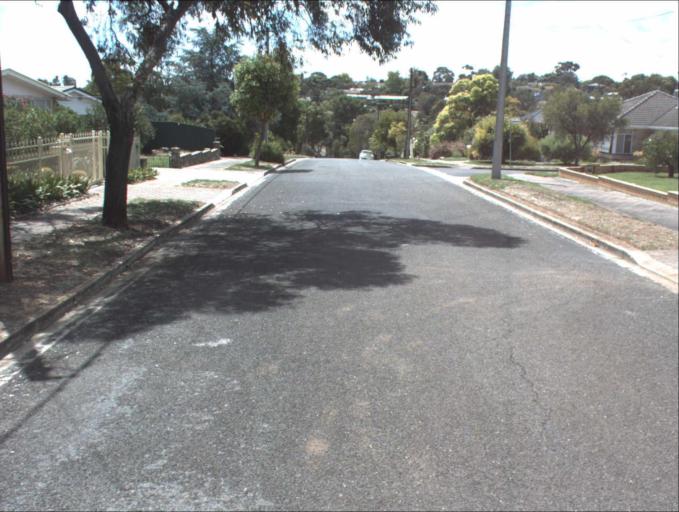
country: AU
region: South Australia
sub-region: Port Adelaide Enfield
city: Gilles Plains
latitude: -34.8421
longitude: 138.6559
